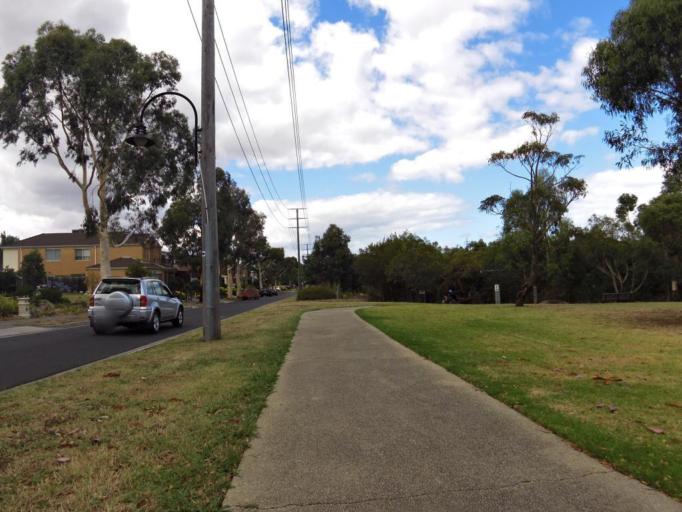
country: AU
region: Victoria
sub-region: Monash
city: Notting Hill
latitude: -37.8952
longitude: 145.1538
